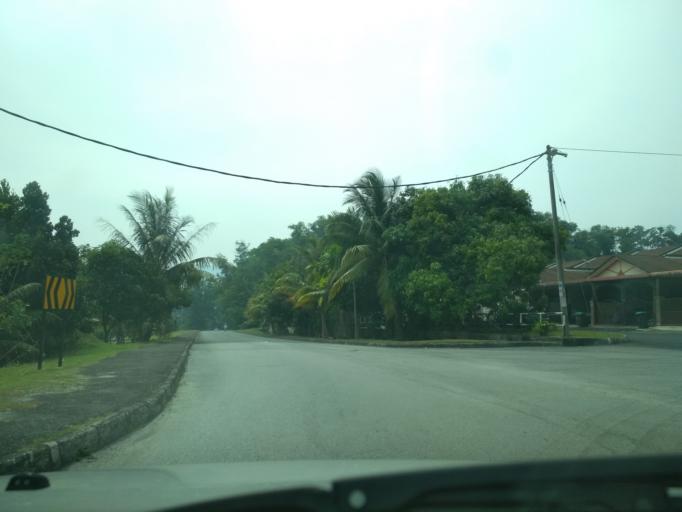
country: MY
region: Kedah
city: Kulim
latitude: 5.3709
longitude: 100.5674
